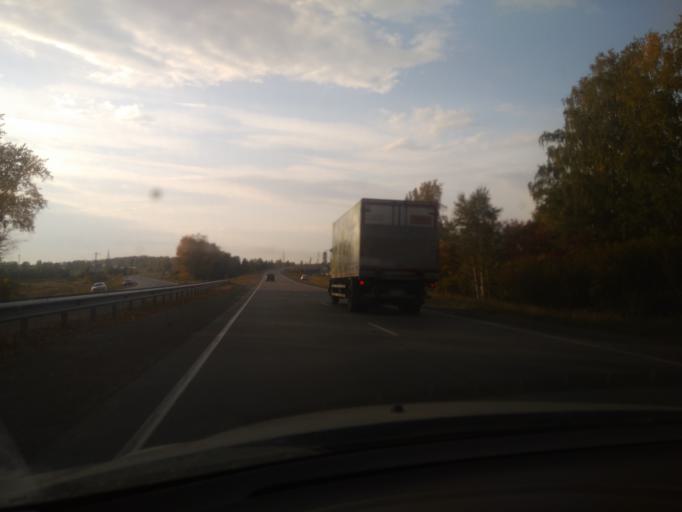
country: RU
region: Sverdlovsk
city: Verkhneye Dubrovo
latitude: 56.7293
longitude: 61.0324
